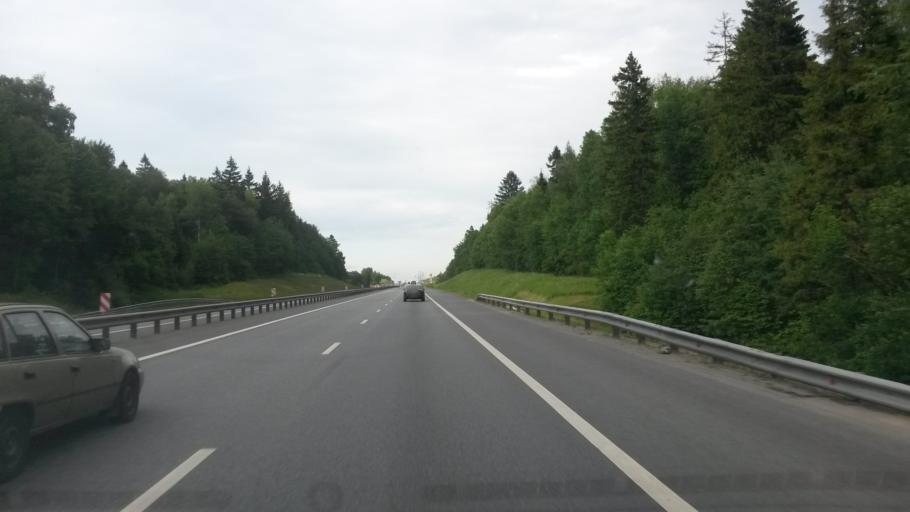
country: RU
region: Moskovskaya
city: Sergiyev Posad
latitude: 56.2286
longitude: 38.1267
